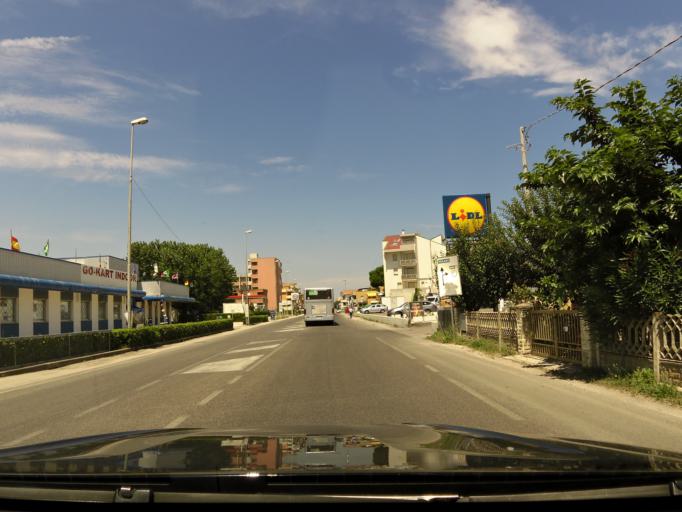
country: IT
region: The Marches
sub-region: Provincia di Pesaro e Urbino
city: Marotta
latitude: 43.7628
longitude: 13.1479
